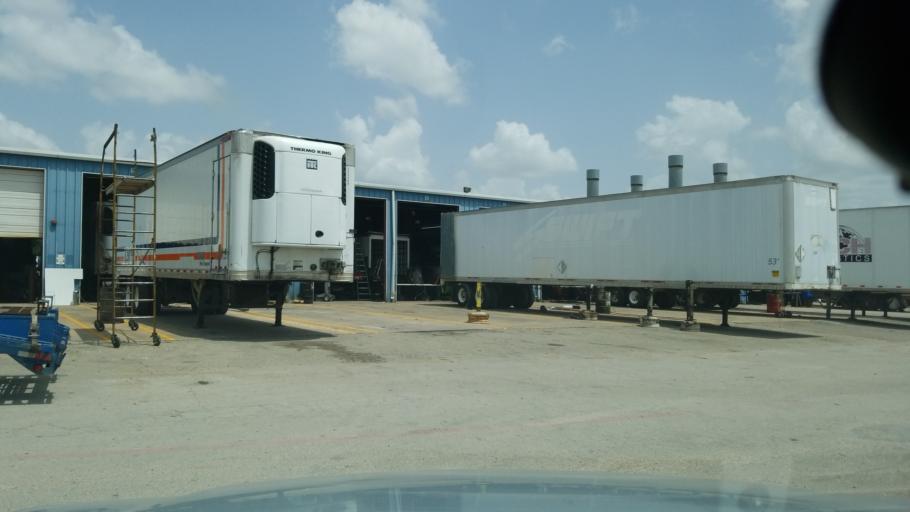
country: US
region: Texas
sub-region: Dallas County
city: Irving
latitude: 32.8284
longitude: -96.9123
